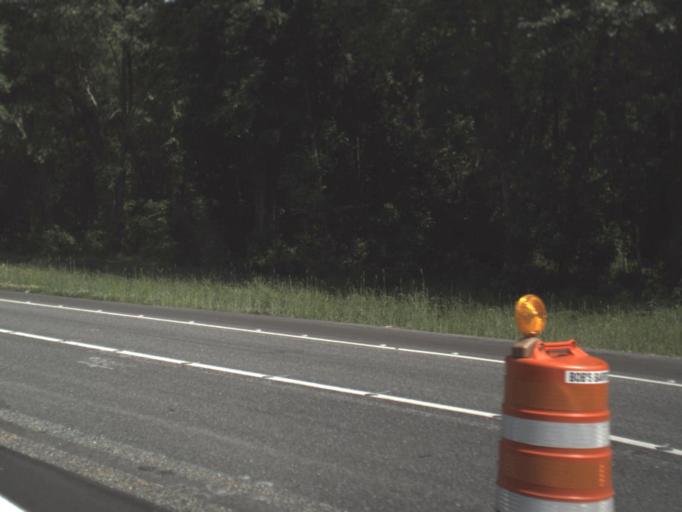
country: US
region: Florida
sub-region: Columbia County
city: Five Points
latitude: 30.2448
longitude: -82.6852
